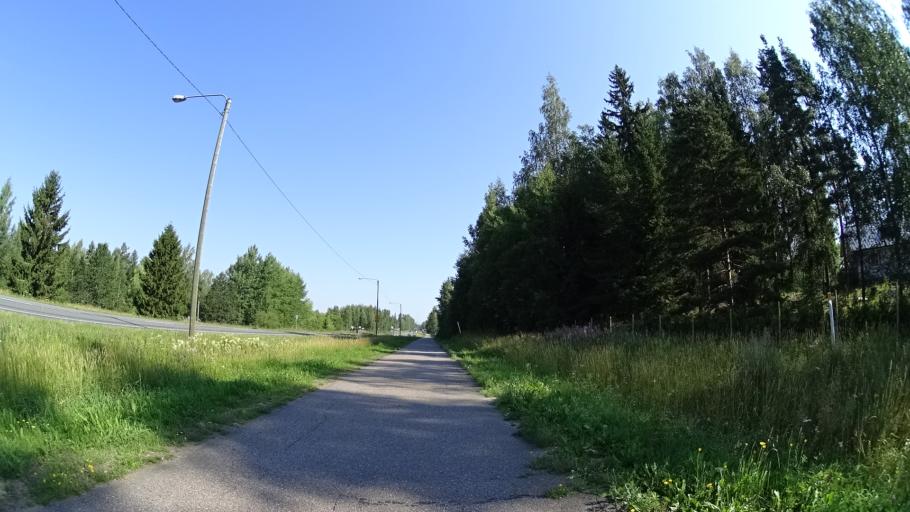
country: FI
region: Uusimaa
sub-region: Helsinki
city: Kerava
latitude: 60.3384
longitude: 25.1253
